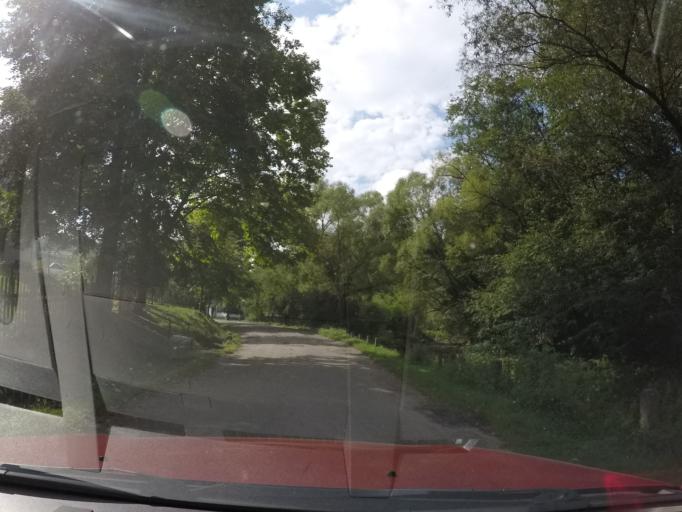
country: UA
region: Zakarpattia
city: Velykyi Bereznyi
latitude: 48.9439
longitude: 22.6218
